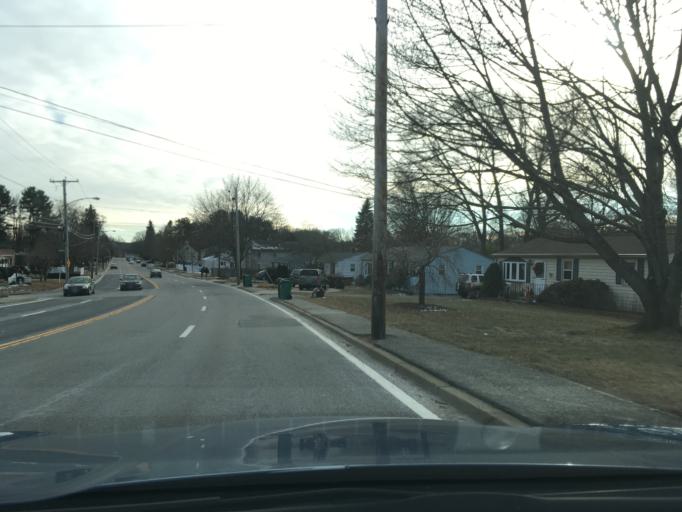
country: US
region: Rhode Island
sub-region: Kent County
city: Warwick
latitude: 41.7106
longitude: -71.4645
